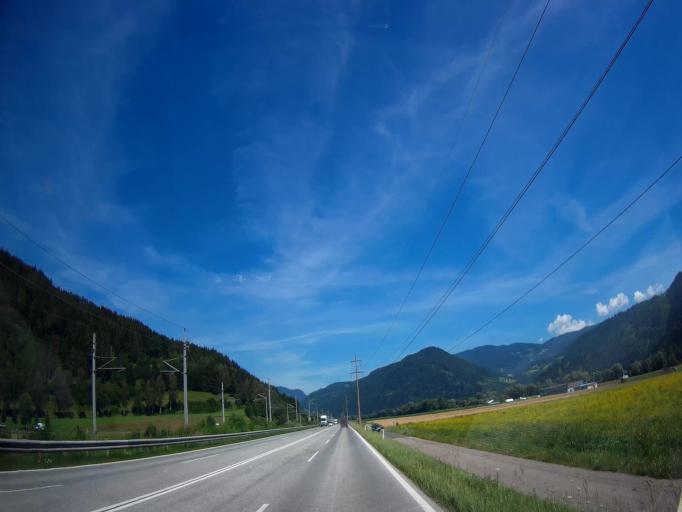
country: AT
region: Carinthia
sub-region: Politischer Bezirk Sankt Veit an der Glan
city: Micheldorf
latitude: 46.9242
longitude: 14.4291
